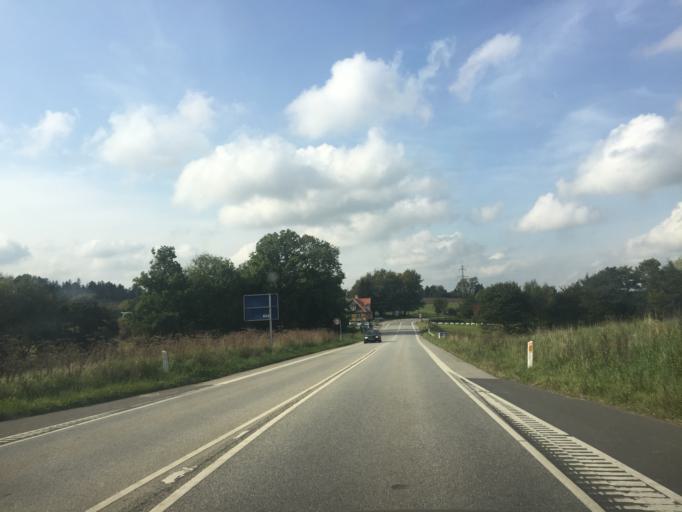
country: DK
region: Zealand
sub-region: Holbaek Kommune
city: Tollose
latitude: 55.6341
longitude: 11.7946
